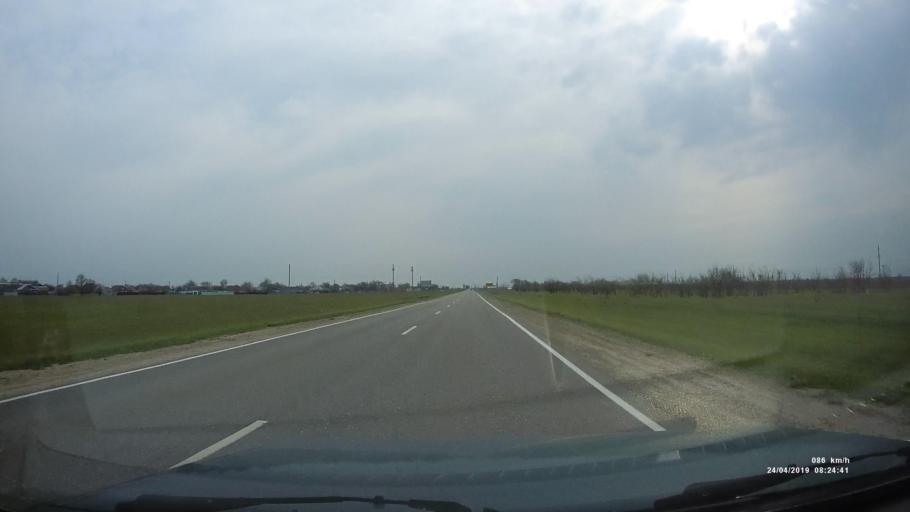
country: RU
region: Kalmykiya
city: Priyutnoye
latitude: 46.1214
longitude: 43.7590
